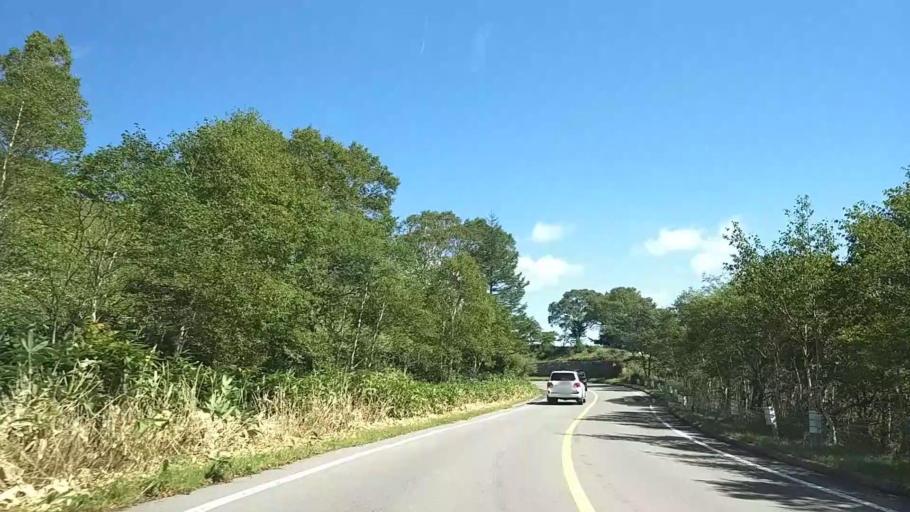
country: JP
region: Nagano
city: Suwa
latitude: 36.1687
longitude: 138.1339
